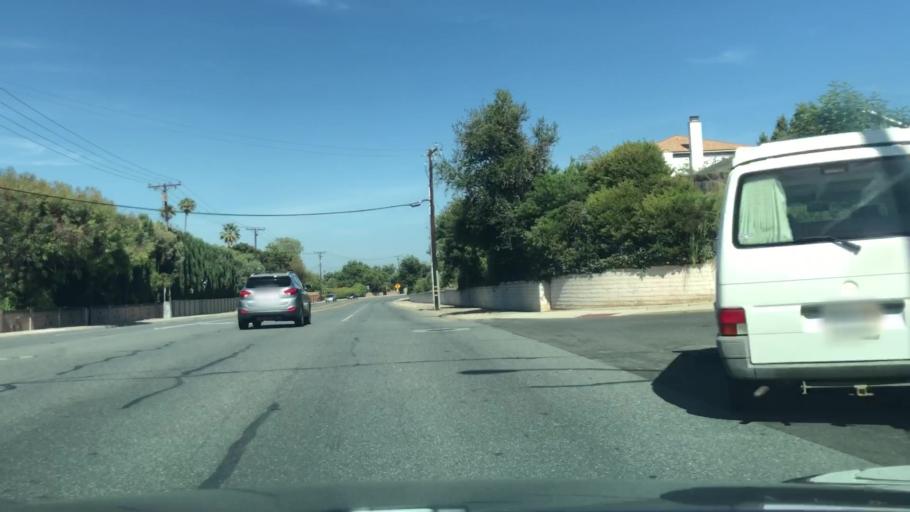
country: US
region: California
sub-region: Ventura County
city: Casa Conejo
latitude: 34.1797
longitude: -118.9475
